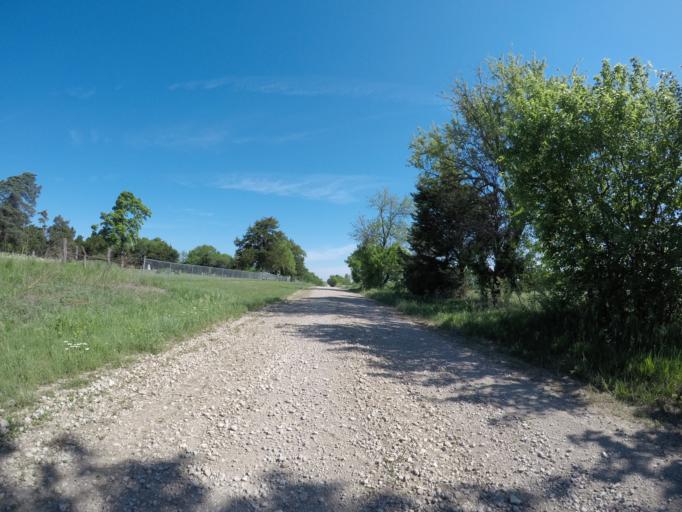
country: US
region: Kansas
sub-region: Wabaunsee County
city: Alma
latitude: 38.9419
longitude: -96.1138
